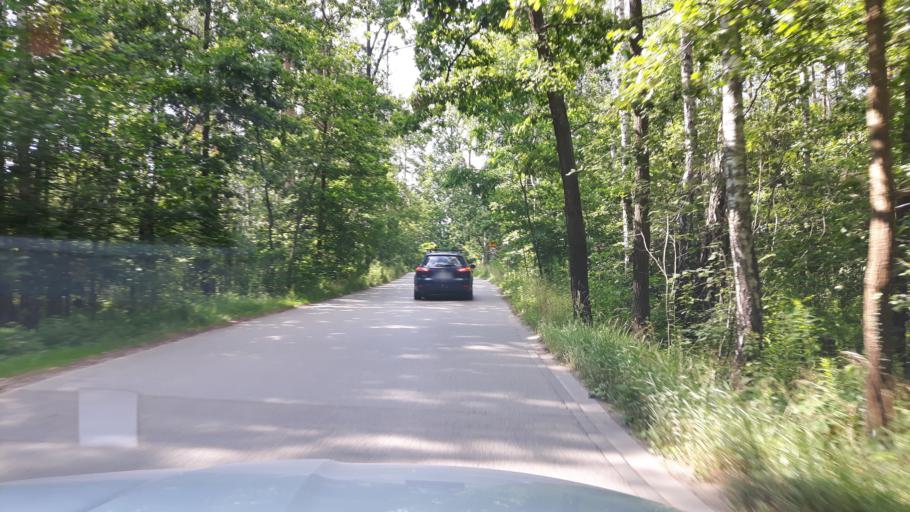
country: PL
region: Masovian Voivodeship
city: Zielonka
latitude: 52.2907
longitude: 21.1650
